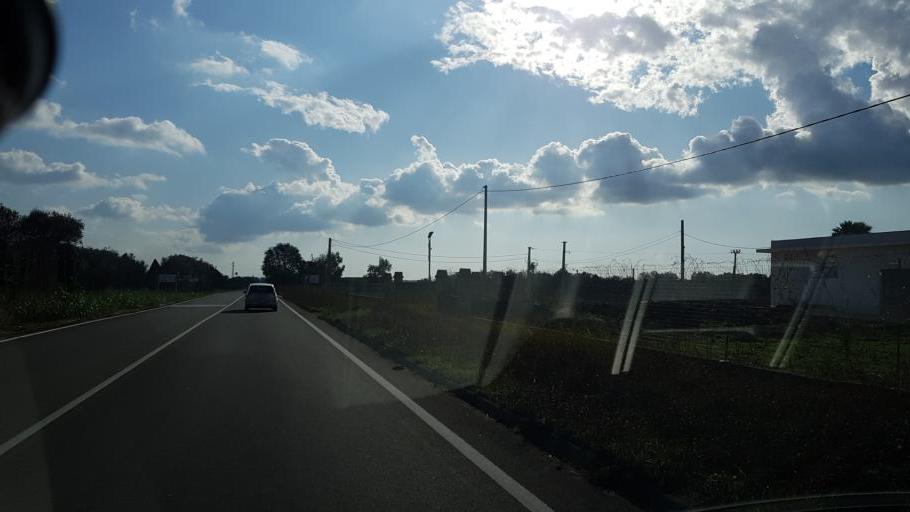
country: IT
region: Apulia
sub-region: Provincia di Lecce
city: Salice Salentino
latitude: 40.3621
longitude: 17.9677
